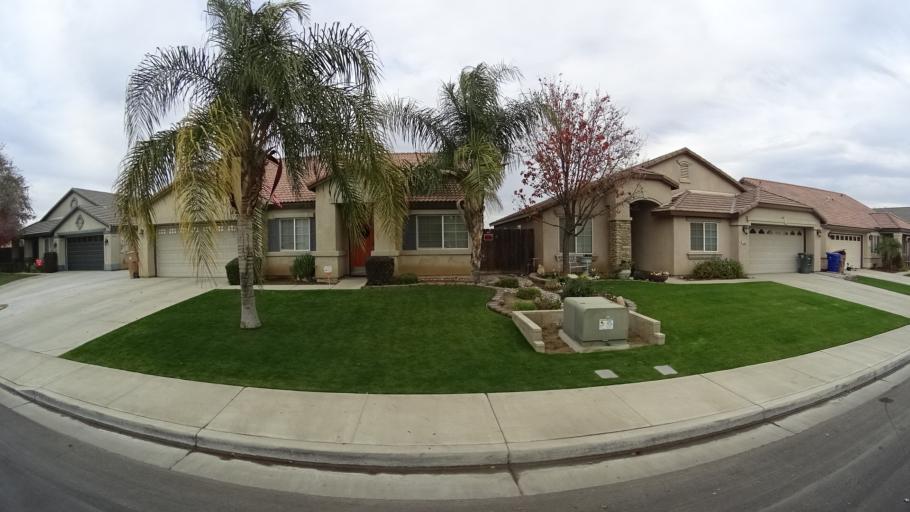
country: US
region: California
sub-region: Kern County
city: Rosedale
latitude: 35.4092
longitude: -119.1511
